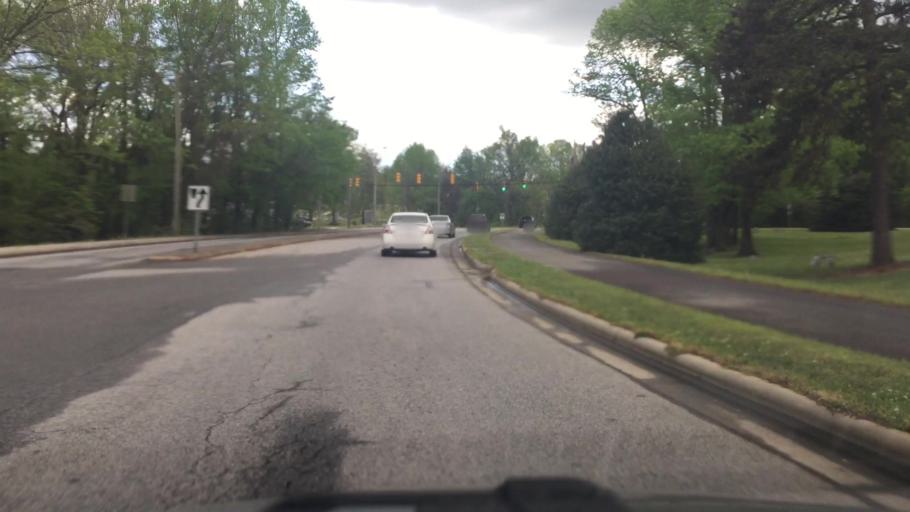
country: US
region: North Carolina
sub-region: Rowan County
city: Salisbury
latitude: 35.6767
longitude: -80.4896
